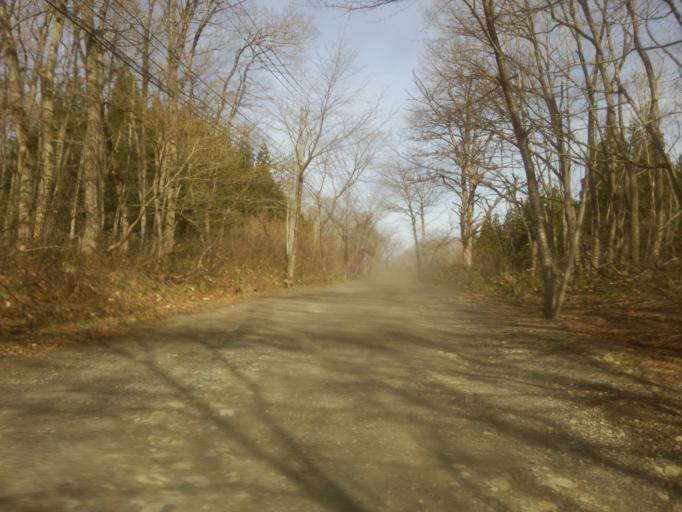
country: JP
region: Fukushima
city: Inawashiro
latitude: 37.5288
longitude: 140.0327
